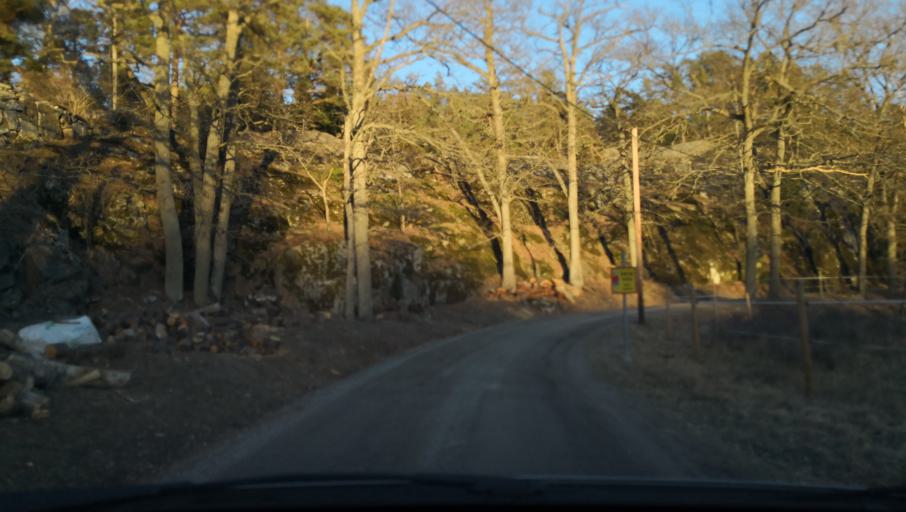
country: SE
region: Stockholm
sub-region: Varmdo Kommun
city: Mortnas
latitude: 59.3360
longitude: 18.4430
